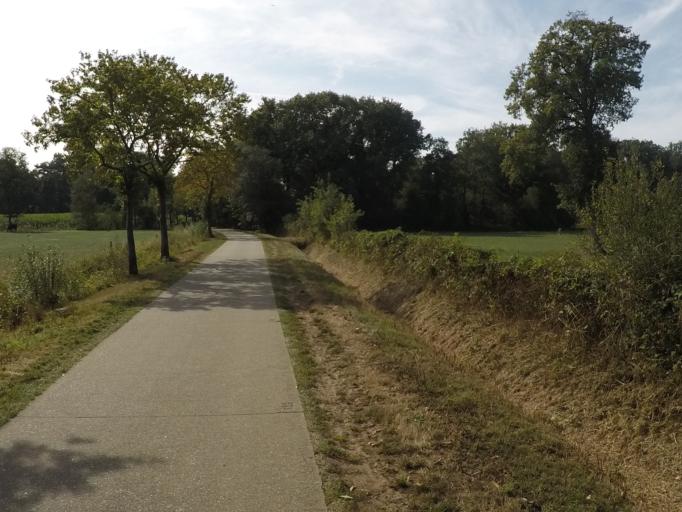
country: BE
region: Flanders
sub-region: Provincie Antwerpen
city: Lille
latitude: 51.2510
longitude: 4.8559
